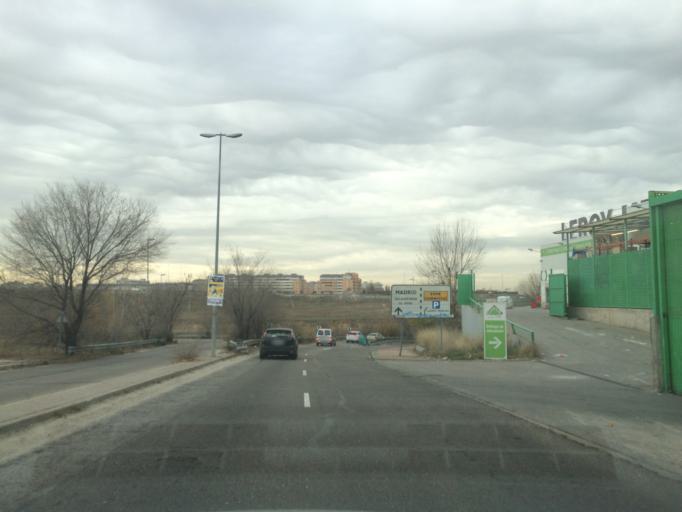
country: ES
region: Madrid
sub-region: Provincia de Madrid
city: Mostoles
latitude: 40.3419
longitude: -3.8498
